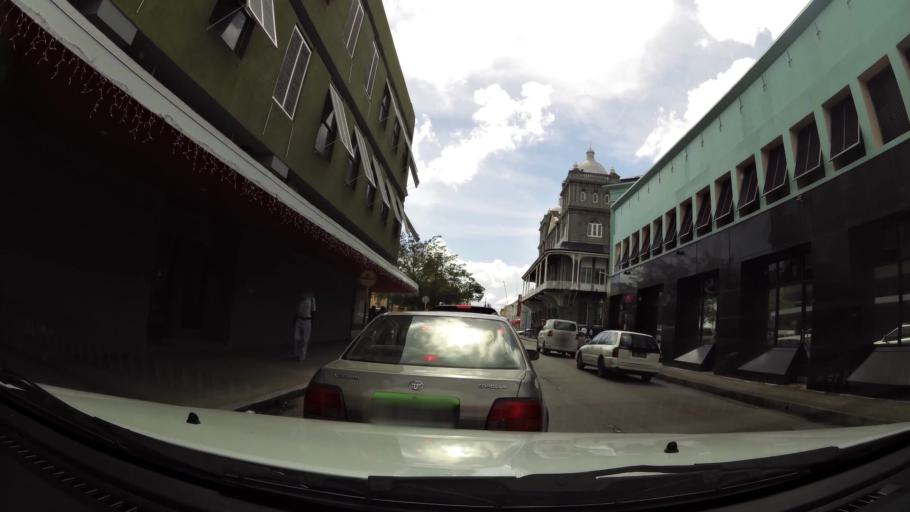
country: BB
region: Saint Michael
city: Bridgetown
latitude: 13.0980
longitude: -59.6174
